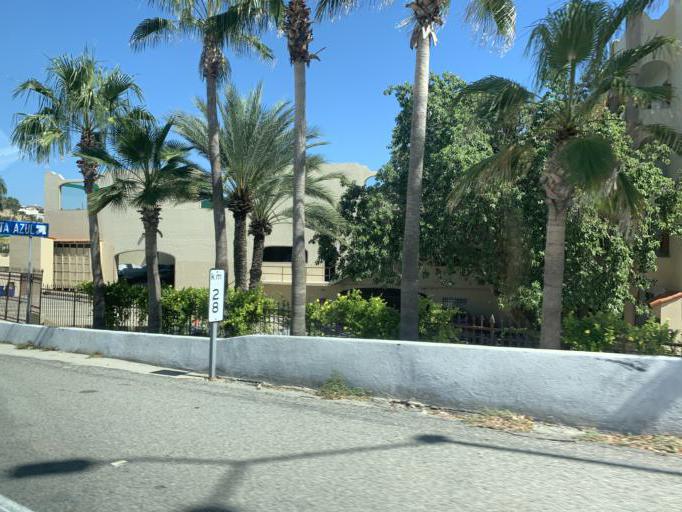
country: MX
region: Baja California Sur
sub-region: Los Cabos
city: San Jose del Cabo
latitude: 23.0273
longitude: -109.7161
